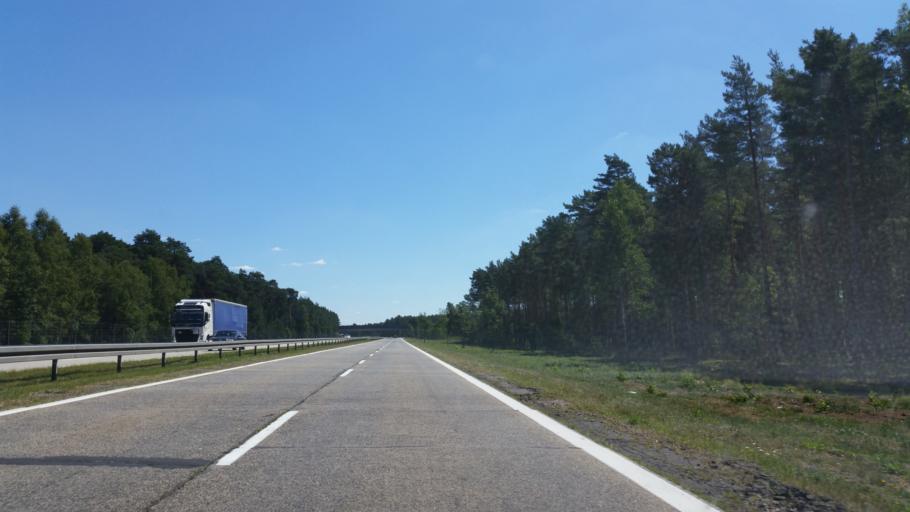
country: PL
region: Lubusz
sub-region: Powiat zaganski
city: Malomice
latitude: 51.4377
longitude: 15.3616
